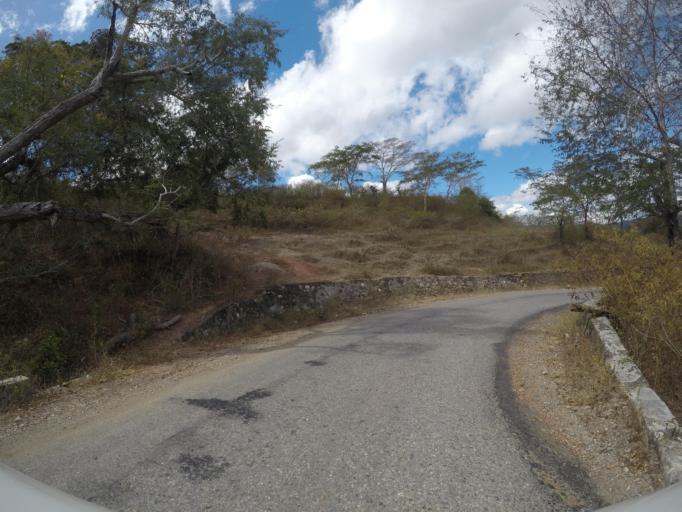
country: TL
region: Lautem
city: Lospalos
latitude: -8.4338
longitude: 126.8316
